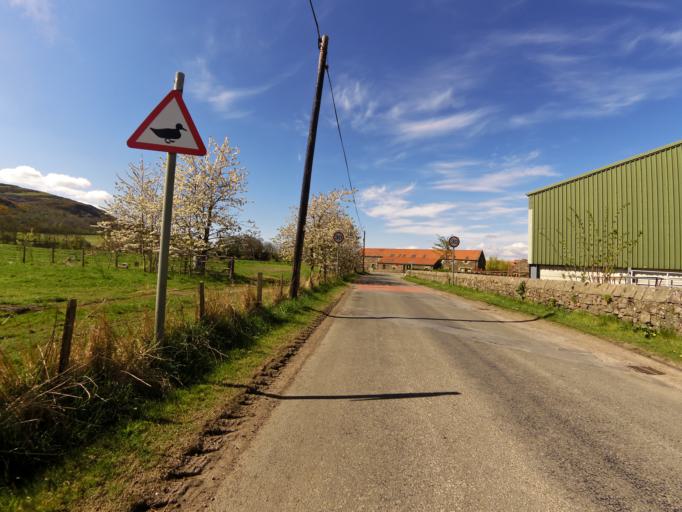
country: GB
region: Scotland
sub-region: Fife
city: Newburgh
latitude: 56.3531
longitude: -3.2206
